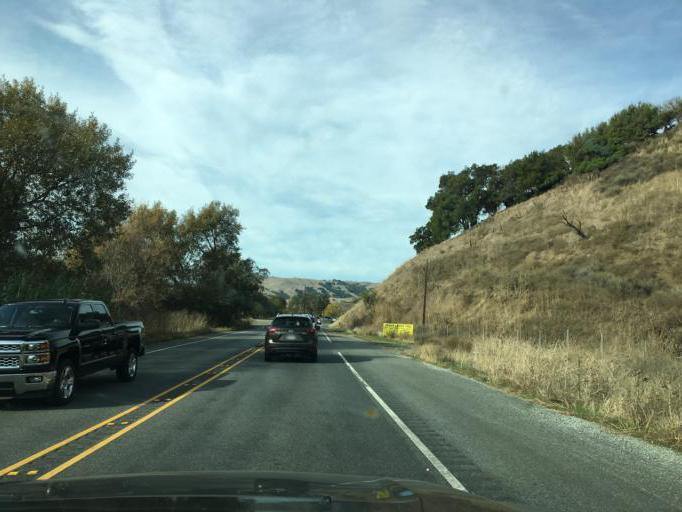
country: US
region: California
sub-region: San Benito County
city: Hollister
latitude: 36.9774
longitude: -121.4366
